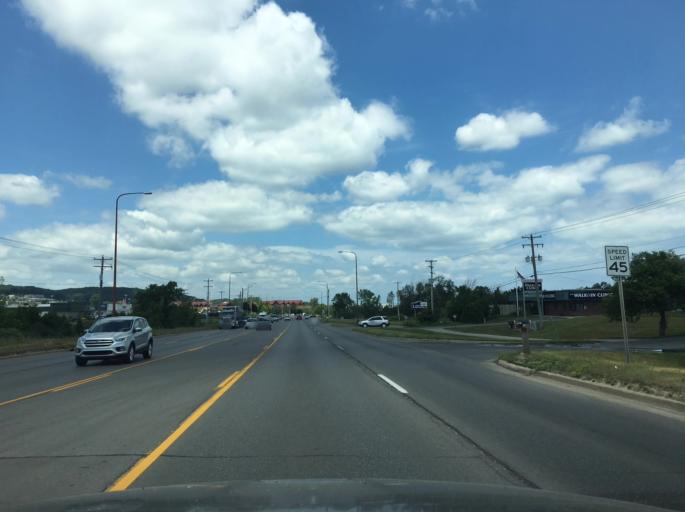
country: US
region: Michigan
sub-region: Grand Traverse County
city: Traverse City
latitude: 44.7301
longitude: -85.6461
